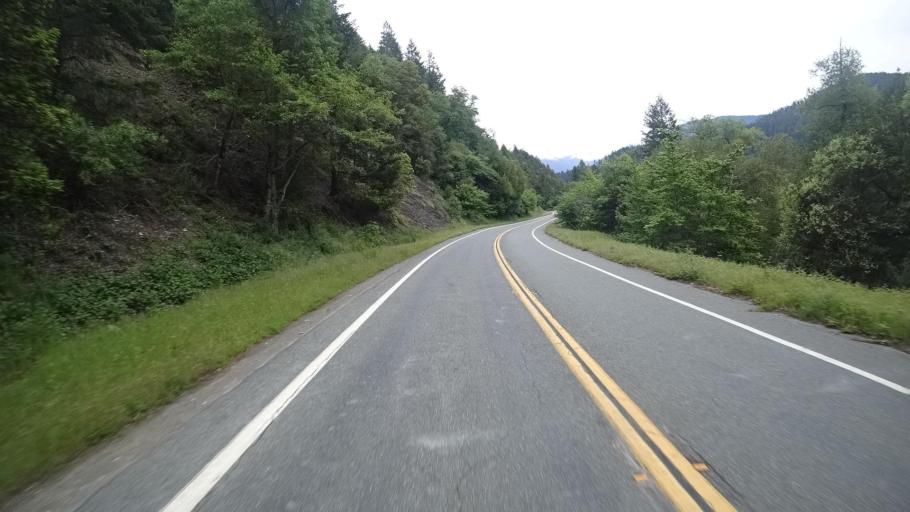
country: US
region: California
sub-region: Humboldt County
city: Willow Creek
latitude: 41.2811
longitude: -123.5848
